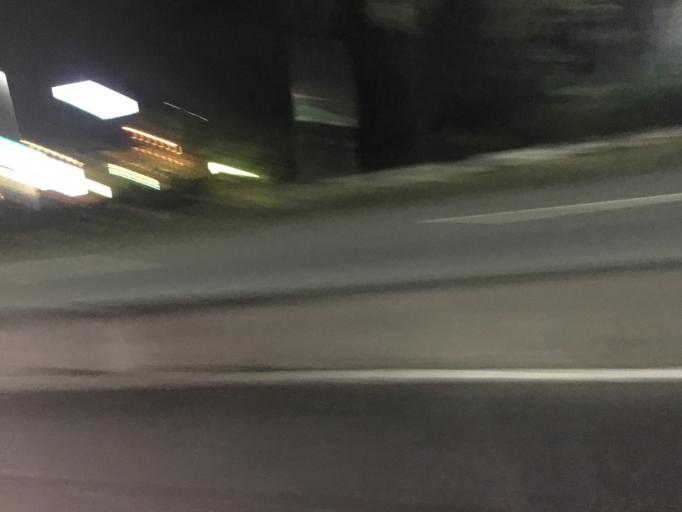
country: TW
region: Taiwan
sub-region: Hsinchu
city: Hsinchu
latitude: 24.7861
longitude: 120.9499
